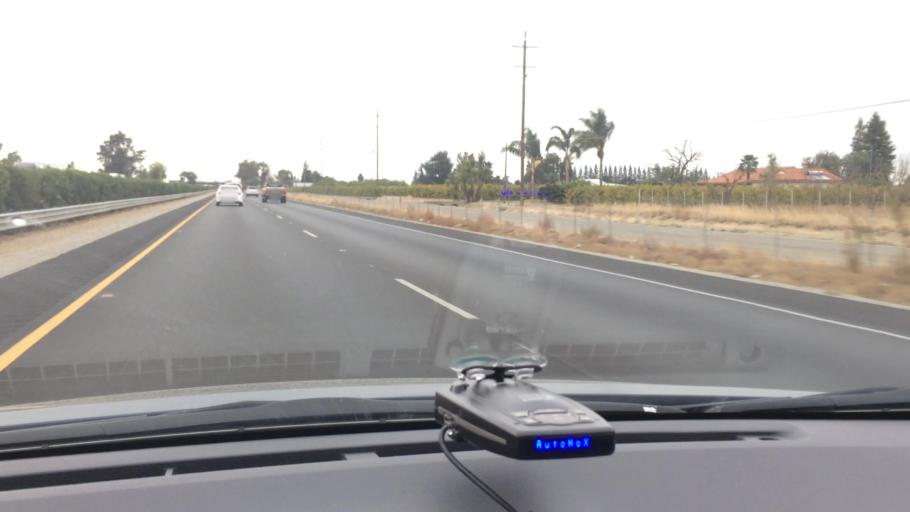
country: US
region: California
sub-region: San Joaquin County
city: Collierville
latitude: 38.1822
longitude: -121.2624
